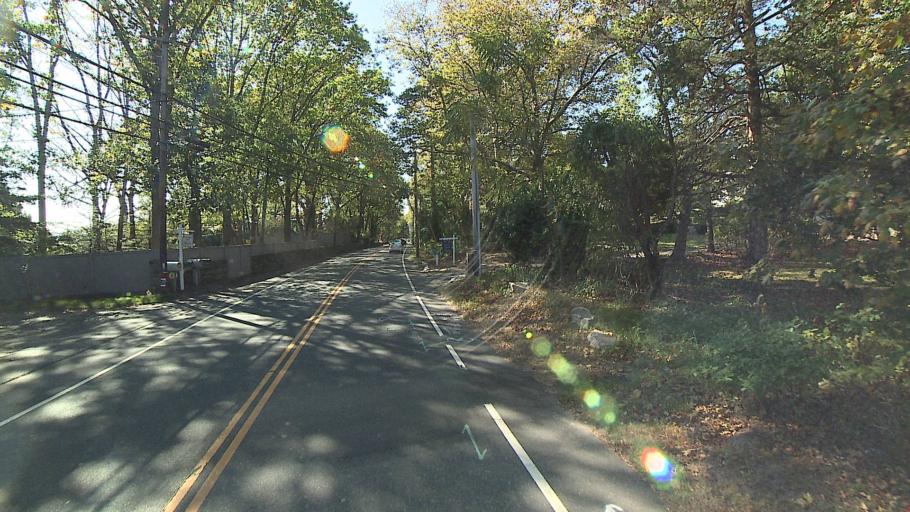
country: US
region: Connecticut
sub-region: Fairfield County
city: East Norwalk
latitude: 41.1137
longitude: -73.3770
